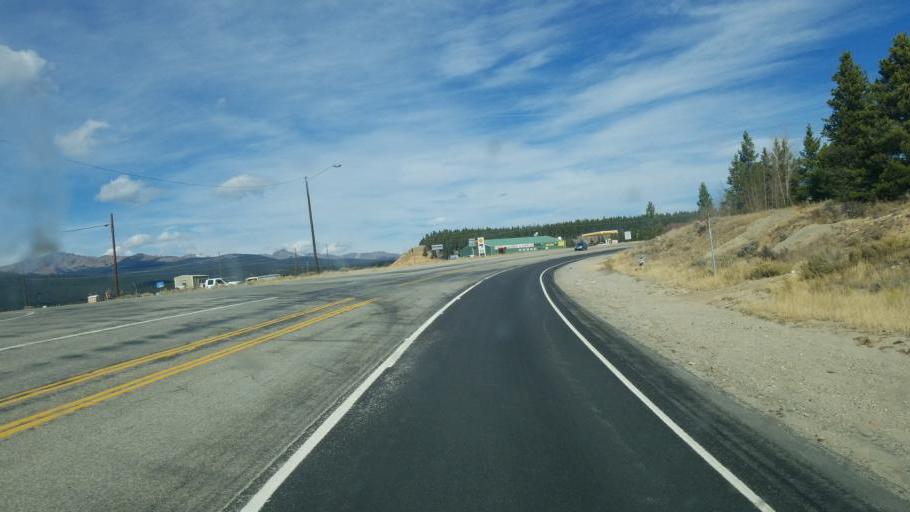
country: US
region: Colorado
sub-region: Lake County
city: Leadville North
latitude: 39.2220
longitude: -106.3486
